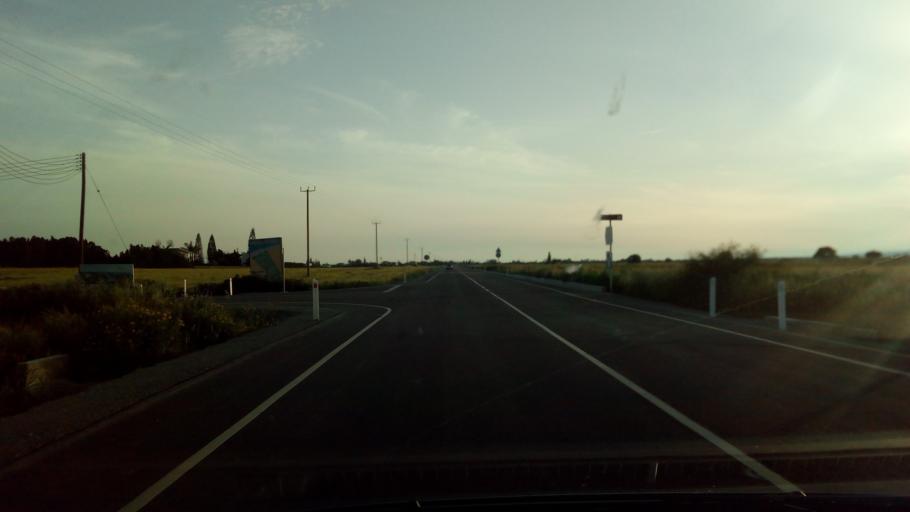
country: CY
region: Larnaka
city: Tersefanou
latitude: 34.8156
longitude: 33.5255
